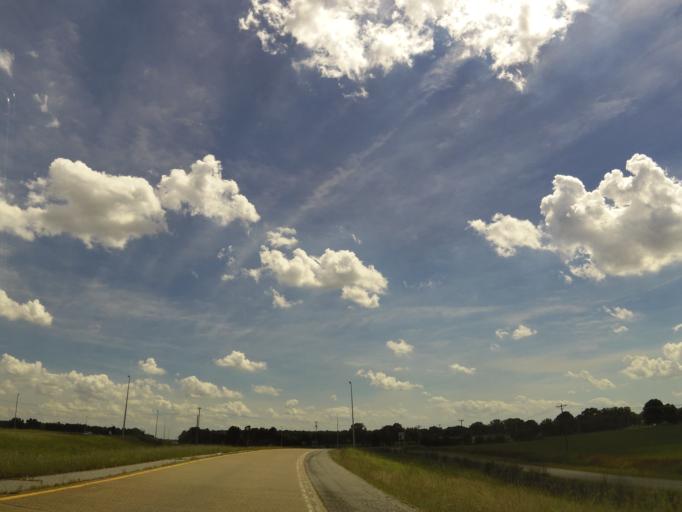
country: US
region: Tennessee
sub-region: Dyer County
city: Dyersburg
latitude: 36.0282
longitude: -89.3408
